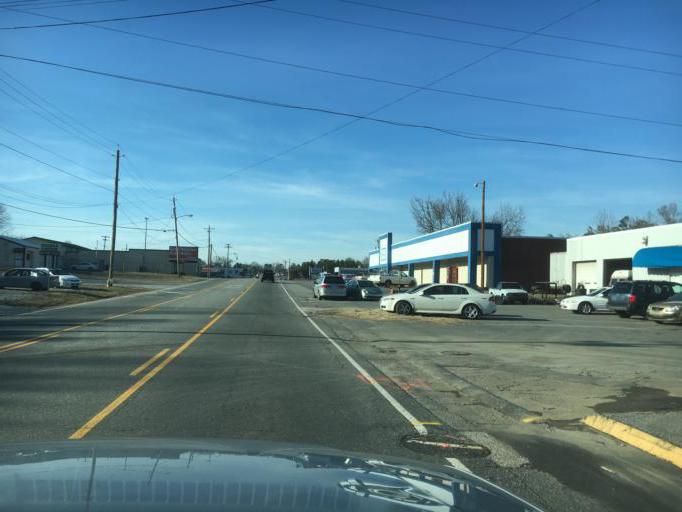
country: US
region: North Carolina
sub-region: Rutherford County
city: Forest City
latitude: 35.3417
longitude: -81.8806
